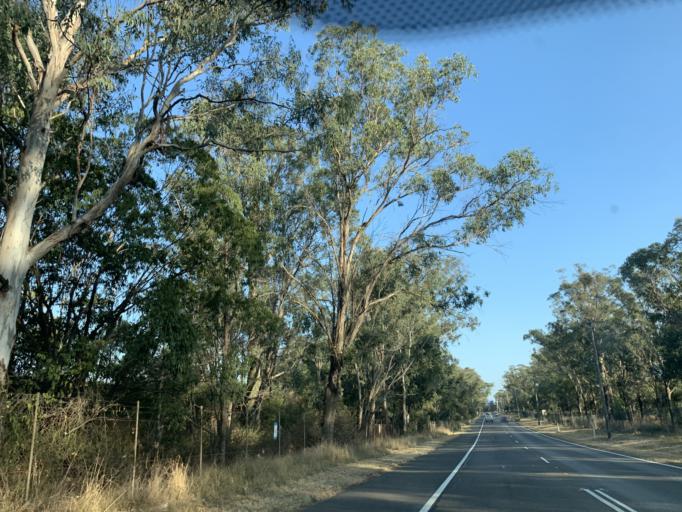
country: AU
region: New South Wales
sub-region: Fairfield
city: Horsley Park
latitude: -33.8278
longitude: 150.8723
